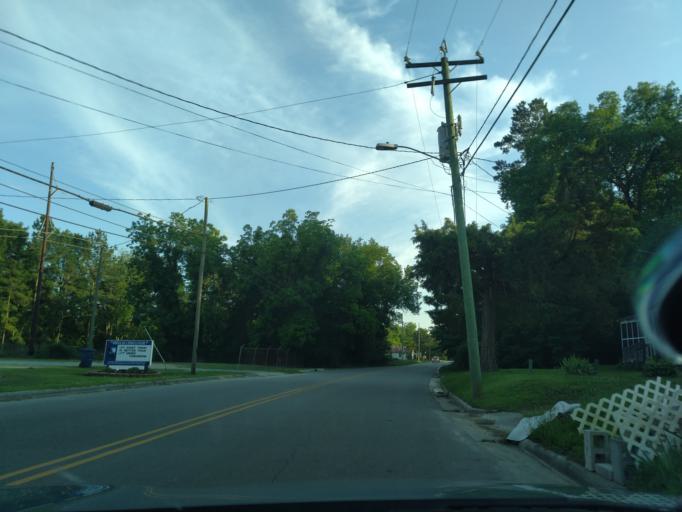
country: US
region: North Carolina
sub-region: Washington County
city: Plymouth
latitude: 35.8570
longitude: -76.7543
